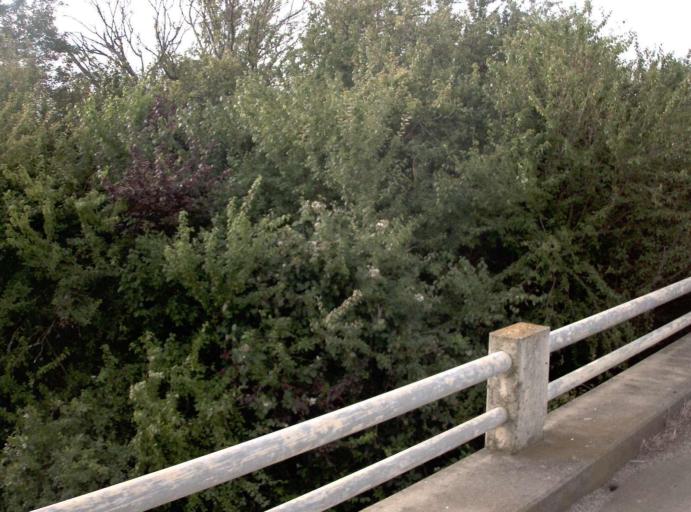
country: AU
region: Victoria
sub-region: Wellington
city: Heyfield
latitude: -37.9742
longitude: 146.8895
